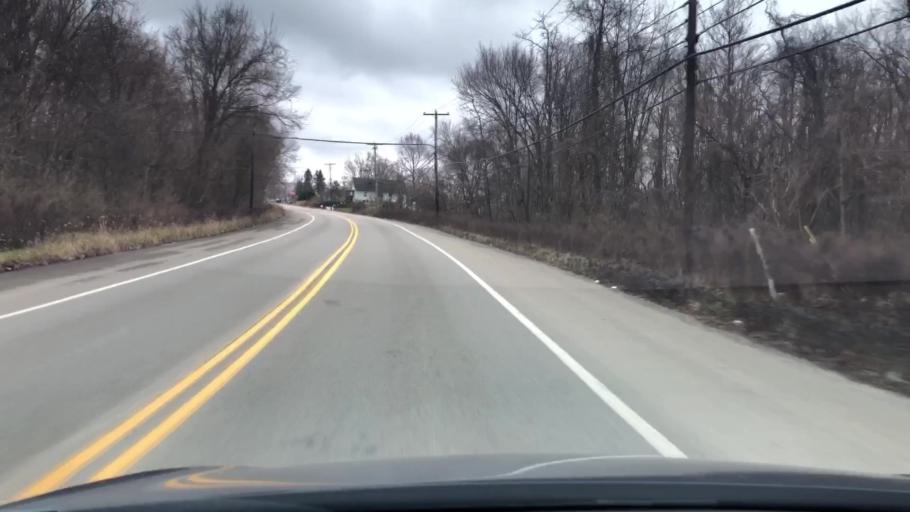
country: US
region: Pennsylvania
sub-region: Fayette County
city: Connellsville
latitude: 40.0331
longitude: -79.5819
